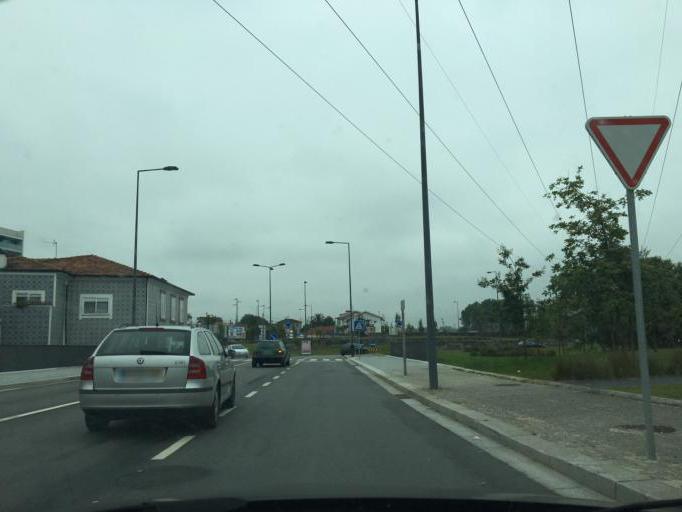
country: PT
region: Porto
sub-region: Maia
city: Nogueira
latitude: 41.2362
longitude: -8.5985
